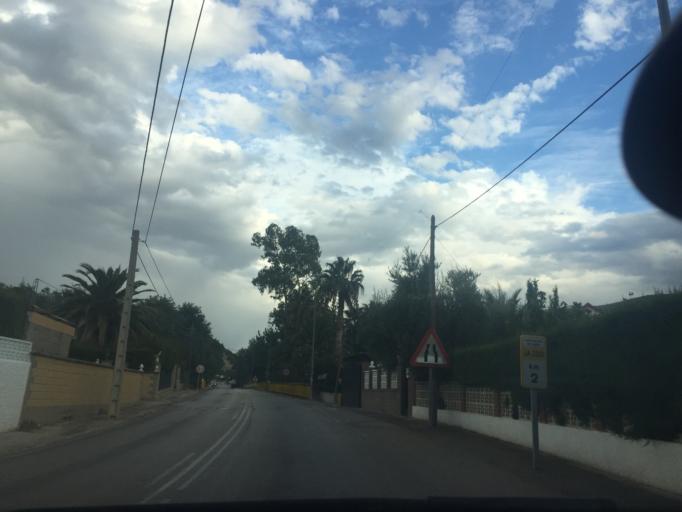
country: ES
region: Andalusia
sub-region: Provincia de Jaen
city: Jaen
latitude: 37.7607
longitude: -3.7528
